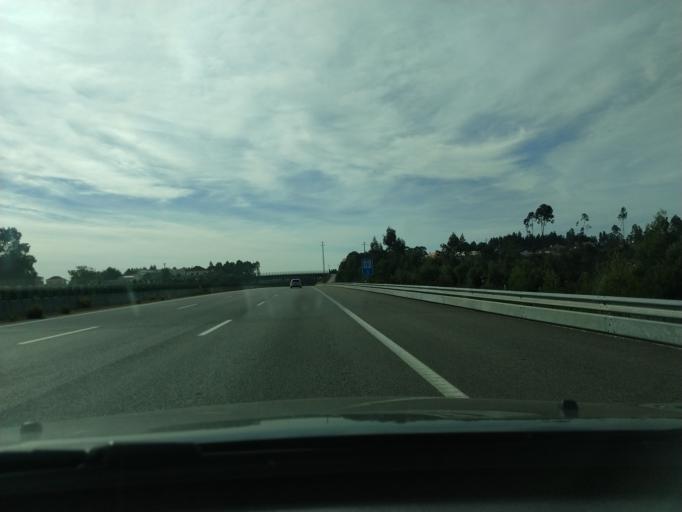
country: PT
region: Aveiro
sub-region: Santa Maria da Feira
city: Feira
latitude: 40.9094
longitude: -8.5676
